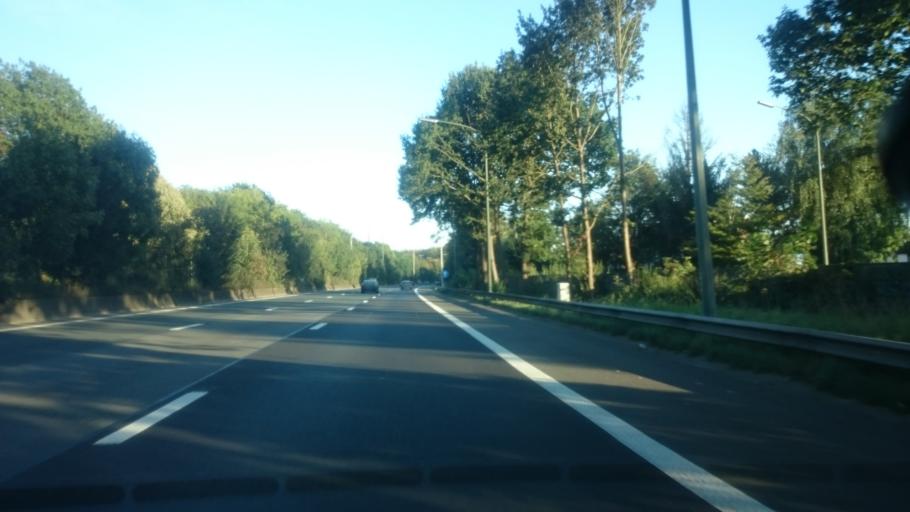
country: BE
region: Flanders
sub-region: Provincie Vlaams-Brabant
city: Hoeilaart
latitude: 50.7915
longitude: 4.4844
